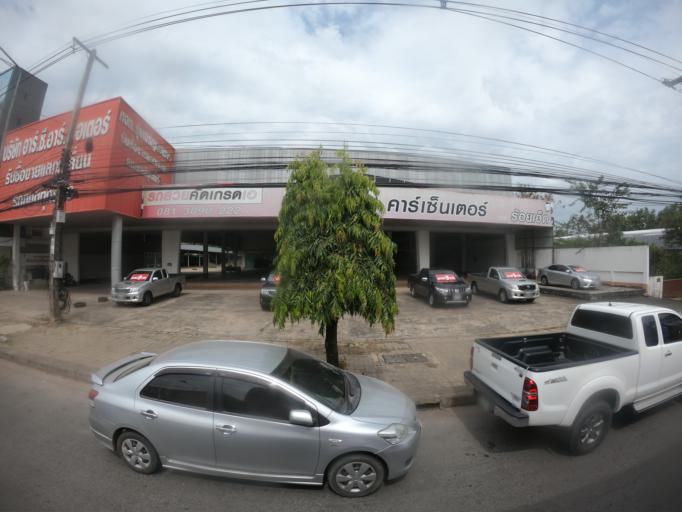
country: TH
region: Roi Et
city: Roi Et
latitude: 16.0596
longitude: 103.6294
